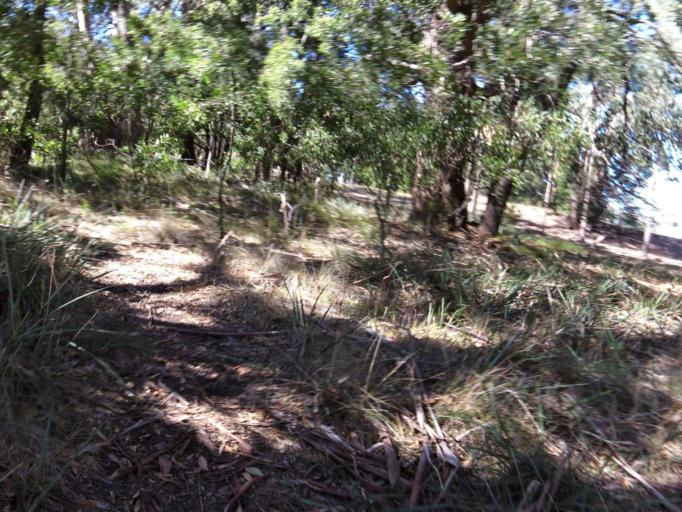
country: AU
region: Victoria
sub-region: Melton
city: Melton West
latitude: -37.5243
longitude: 144.5637
